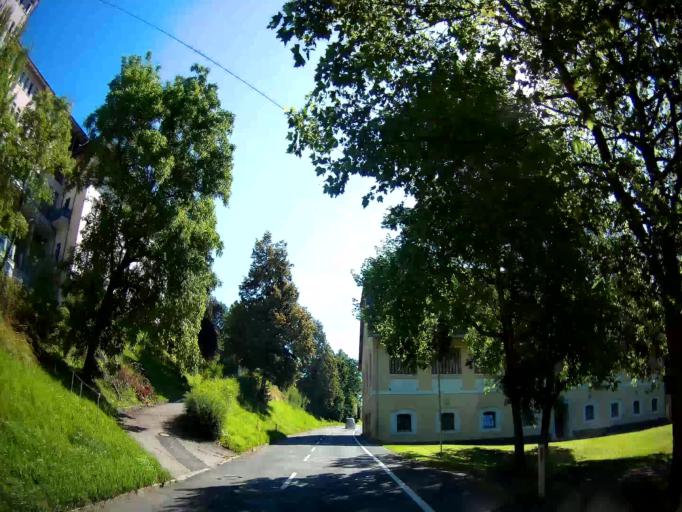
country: AT
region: Carinthia
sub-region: Politischer Bezirk Klagenfurt Land
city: Grafenstein
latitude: 46.6351
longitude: 14.5416
